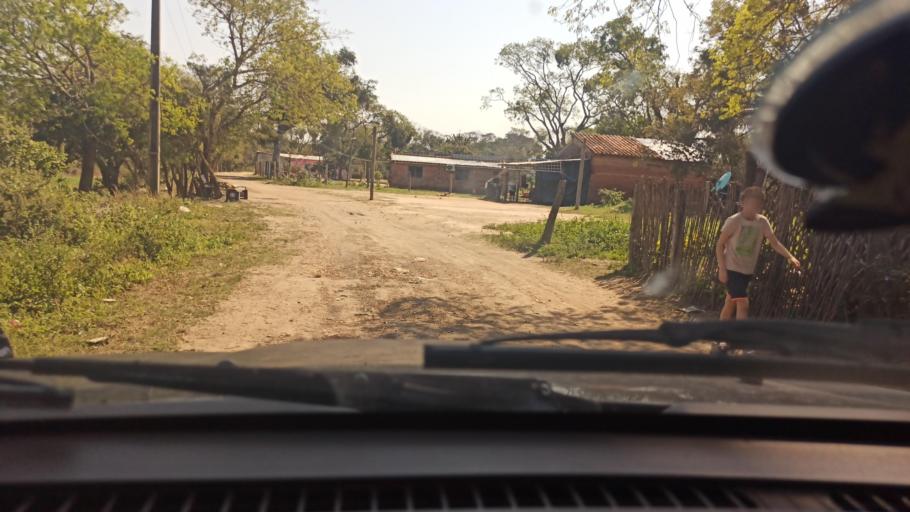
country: PY
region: Asuncion
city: Asuncion
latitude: -25.3323
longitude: -57.6828
